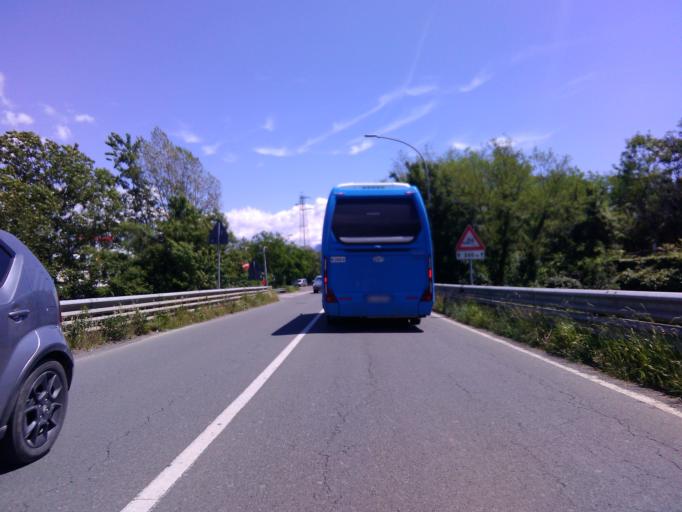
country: IT
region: Tuscany
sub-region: Provincia di Massa-Carrara
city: Terrarossa
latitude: 44.2266
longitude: 9.9667
